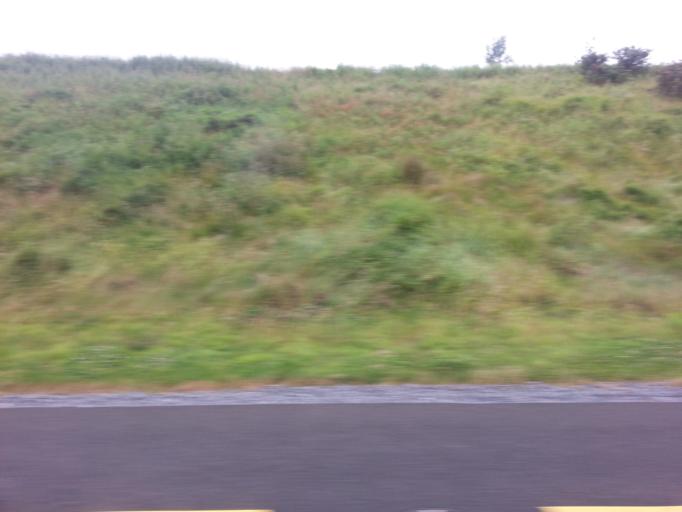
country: IE
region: Leinster
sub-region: Kilkenny
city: Kilkenny
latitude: 52.6459
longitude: -7.1871
